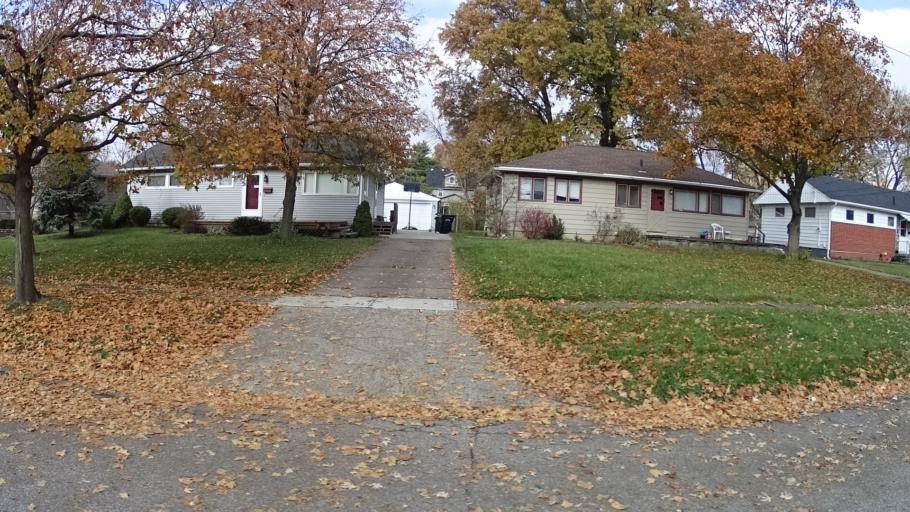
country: US
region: Ohio
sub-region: Lorain County
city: Elyria
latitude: 41.3779
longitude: -82.0925
